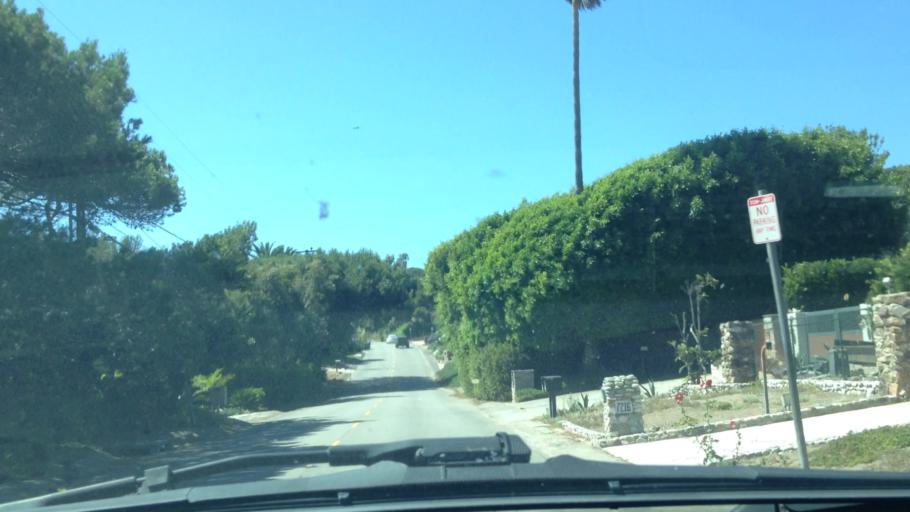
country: US
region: California
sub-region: Los Angeles County
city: Malibu
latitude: 34.0064
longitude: -118.8102
